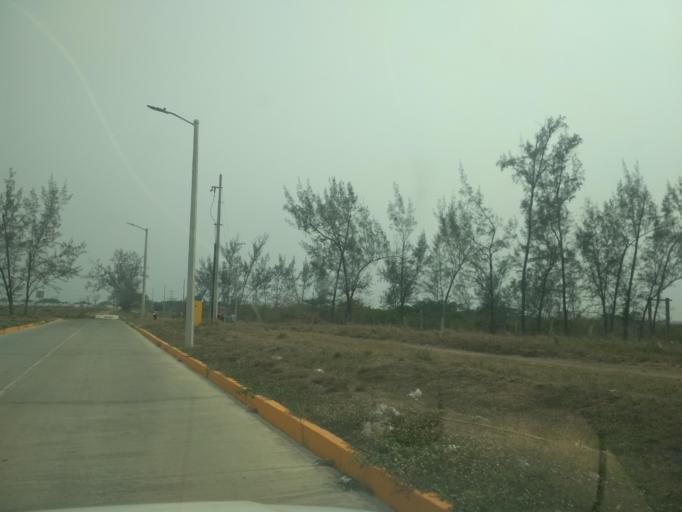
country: MX
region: Veracruz
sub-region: Veracruz
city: Las Amapolas
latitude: 19.1433
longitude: -96.2238
